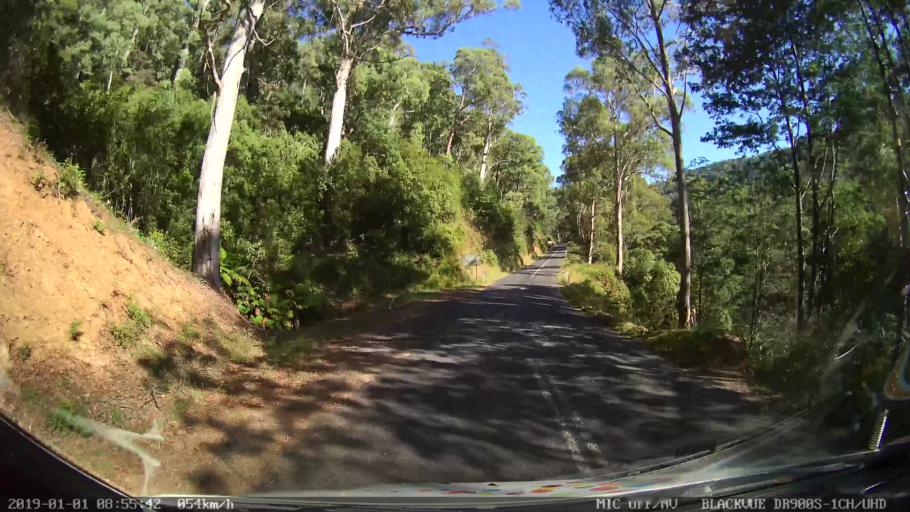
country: AU
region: New South Wales
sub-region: Snowy River
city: Jindabyne
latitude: -36.2521
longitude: 148.1909
